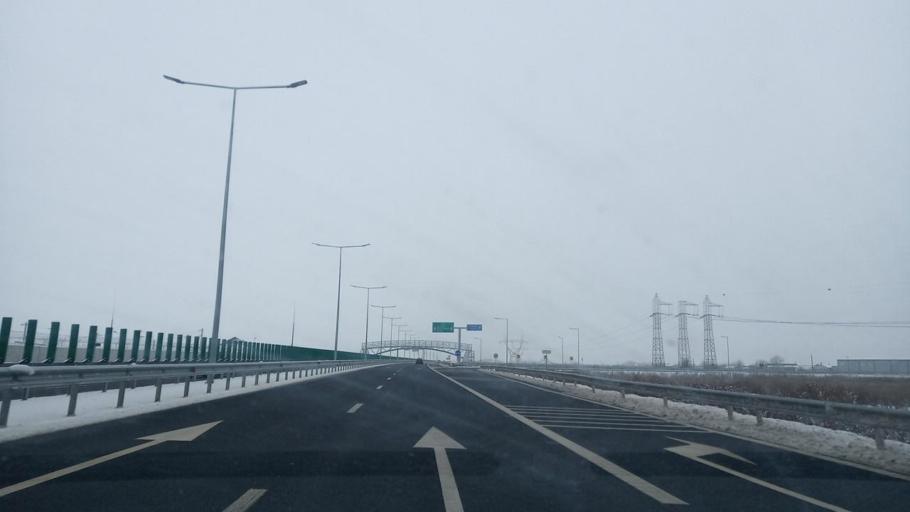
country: RO
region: Bacau
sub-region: Comuna Letea Veche
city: Holt
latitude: 46.5882
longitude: 26.9619
